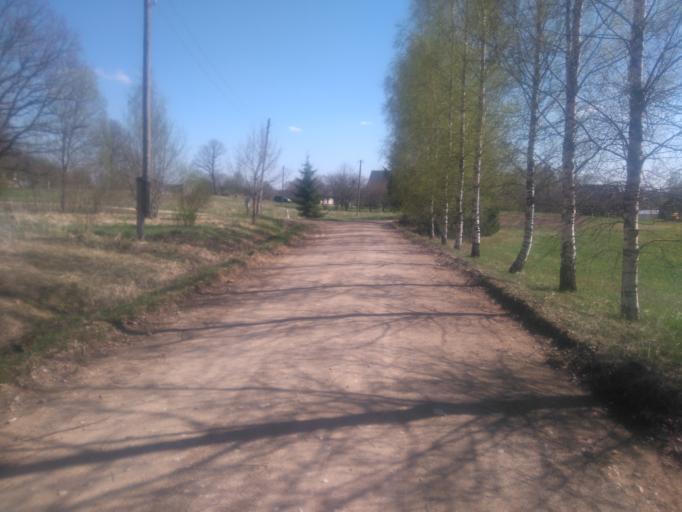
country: LV
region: Vecpiebalga
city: Vecpiebalga
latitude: 57.0266
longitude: 25.8458
